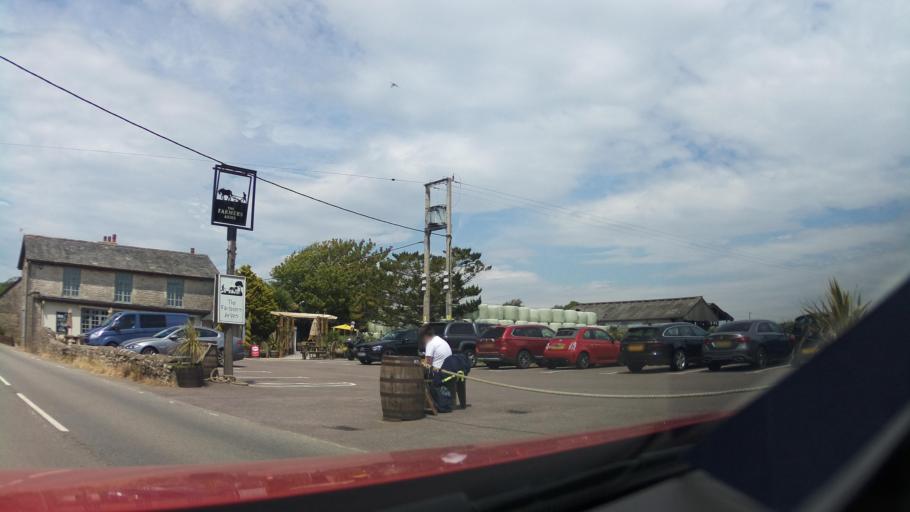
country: GB
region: Wales
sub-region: Bridgend county borough
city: Merthyr Mawr
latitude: 51.4570
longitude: -3.5896
